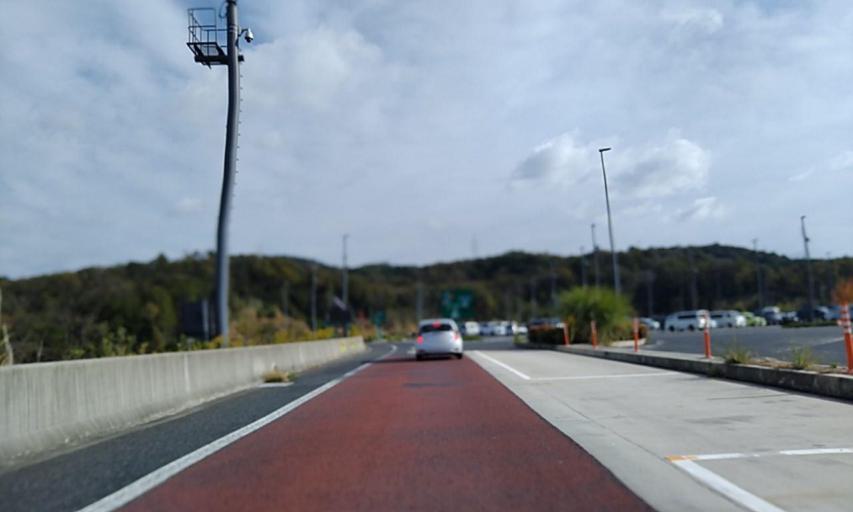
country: JP
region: Aichi
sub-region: Toyota-shi
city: Toyota
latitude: 35.0355
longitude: 137.2222
